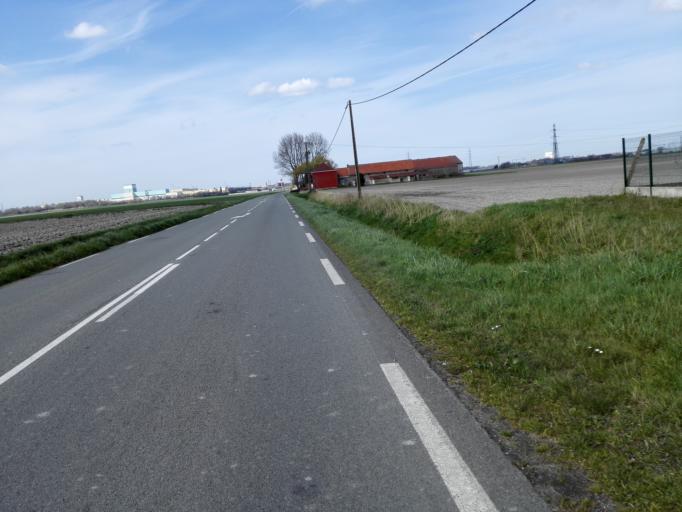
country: FR
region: Nord-Pas-de-Calais
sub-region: Departement du Nord
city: Spycker
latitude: 50.9750
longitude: 2.3112
